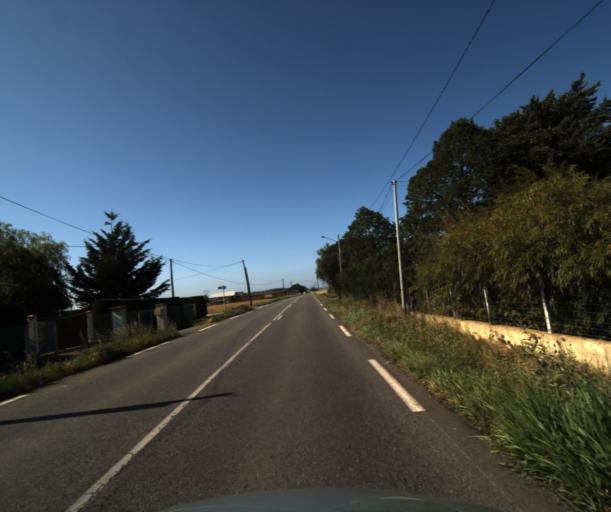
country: FR
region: Midi-Pyrenees
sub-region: Departement de la Haute-Garonne
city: Lagardelle-sur-Leze
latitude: 43.4304
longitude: 1.3784
